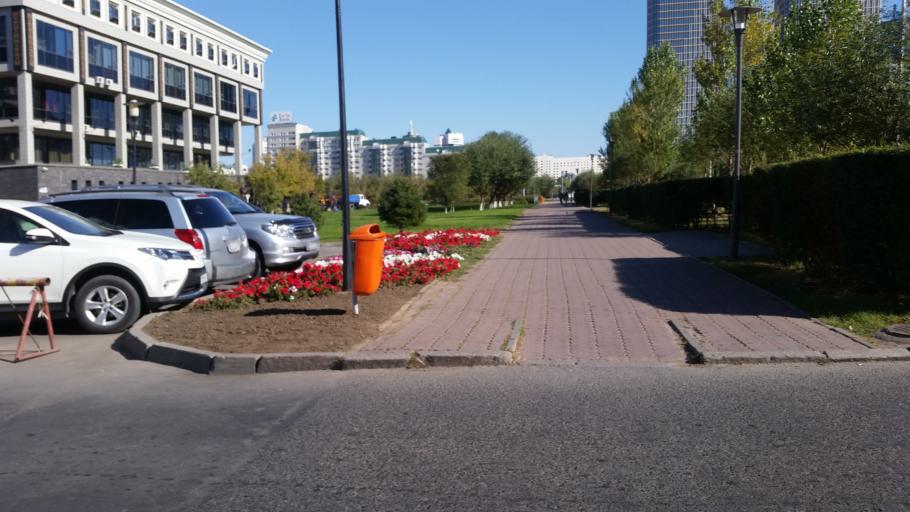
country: KZ
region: Astana Qalasy
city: Astana
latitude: 51.1267
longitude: 71.4260
